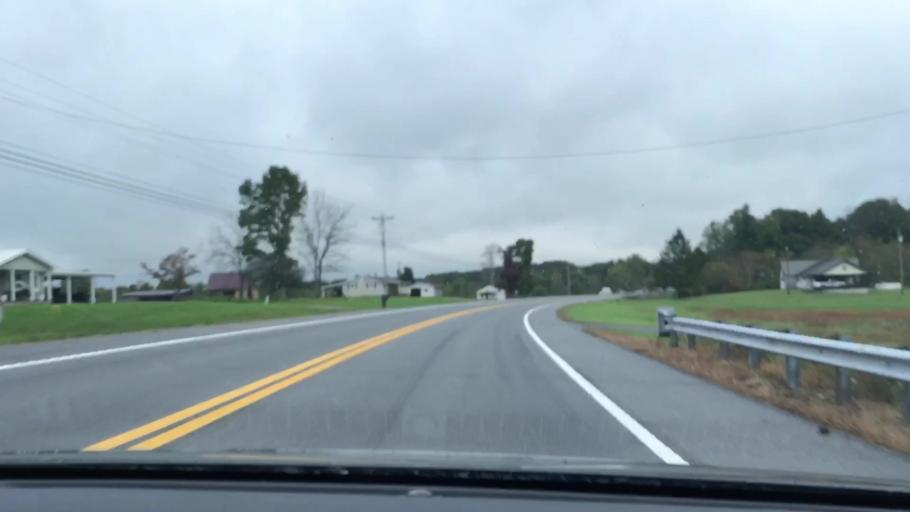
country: US
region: Tennessee
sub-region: Fentress County
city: Grimsley
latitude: 36.2797
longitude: -84.9816
